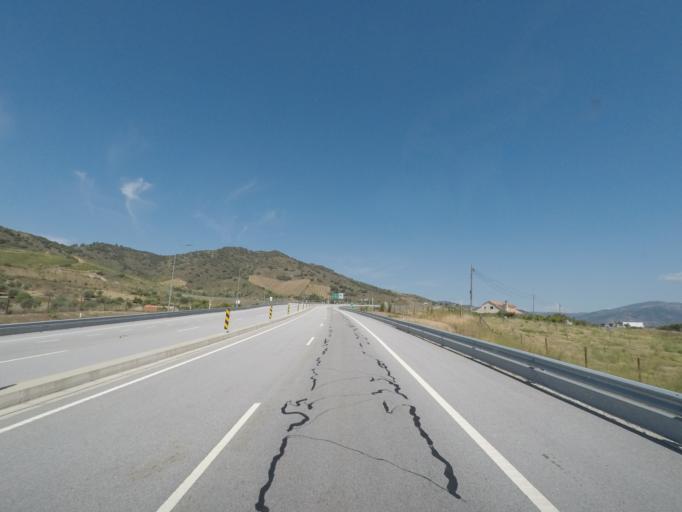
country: PT
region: Braganca
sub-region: Braganca Municipality
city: Vila Flor
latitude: 41.3206
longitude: -7.0789
